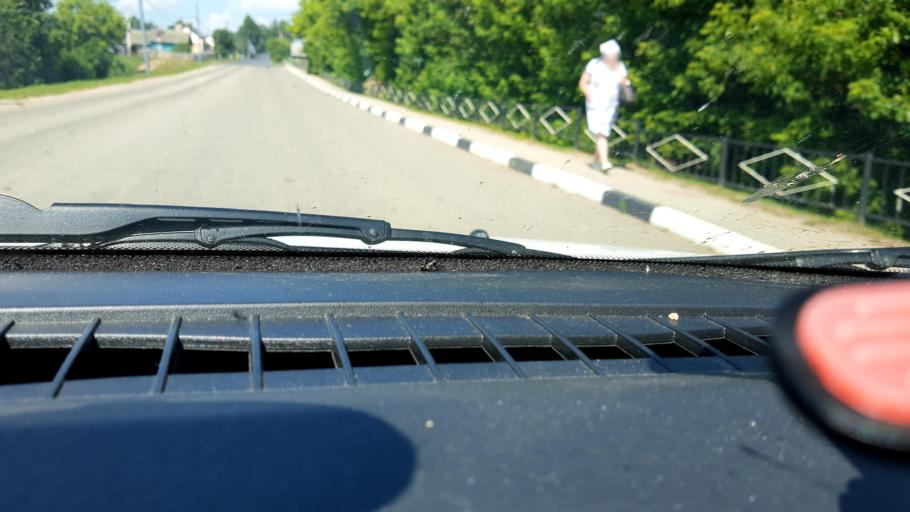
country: RU
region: Nizjnij Novgorod
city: Sharanga
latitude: 57.1694
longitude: 46.5411
